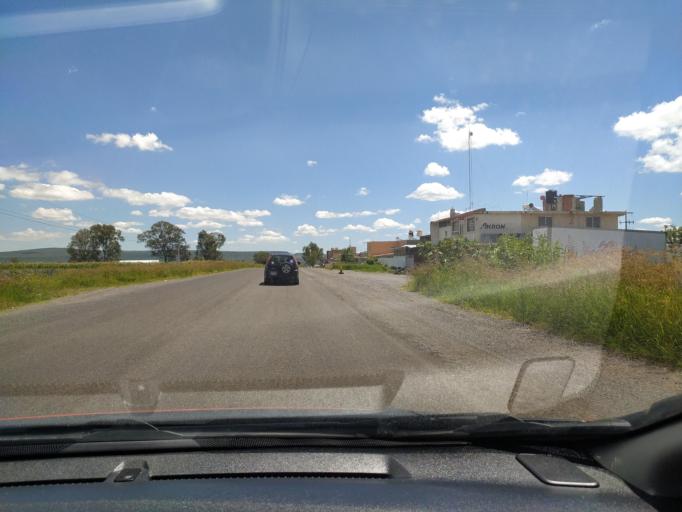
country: MX
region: Jalisco
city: San Diego de Alejandria
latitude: 20.9988
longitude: -102.0036
